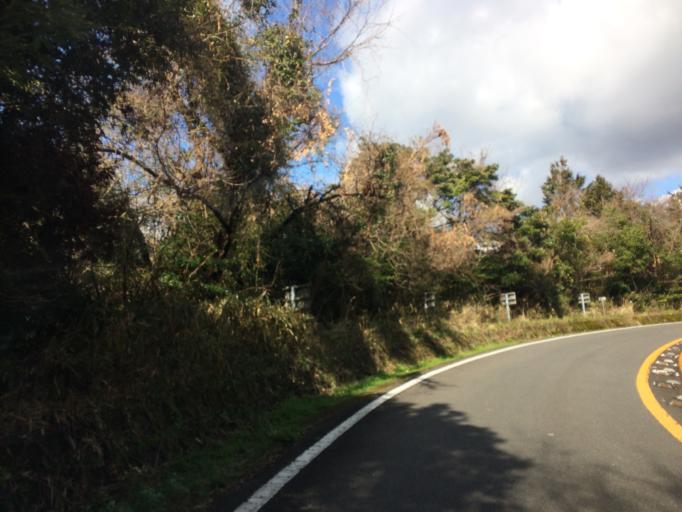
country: JP
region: Shizuoka
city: Shizuoka-shi
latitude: 34.9649
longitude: 138.4482
